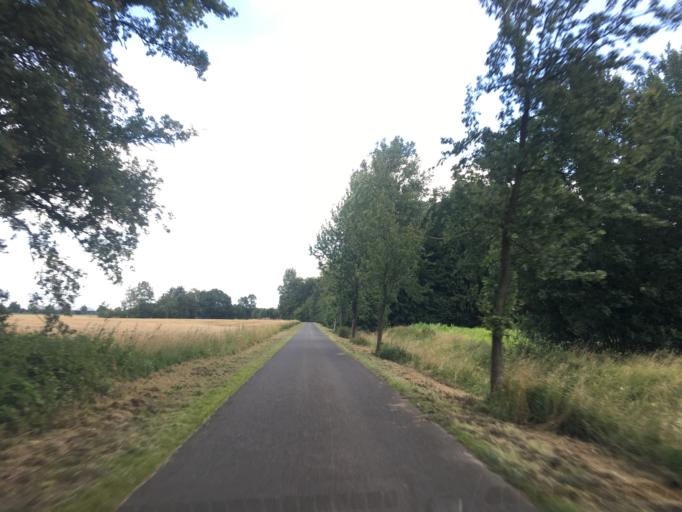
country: DE
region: North Rhine-Westphalia
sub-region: Regierungsbezirk Munster
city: Muenster
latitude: 52.0226
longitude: 7.5917
